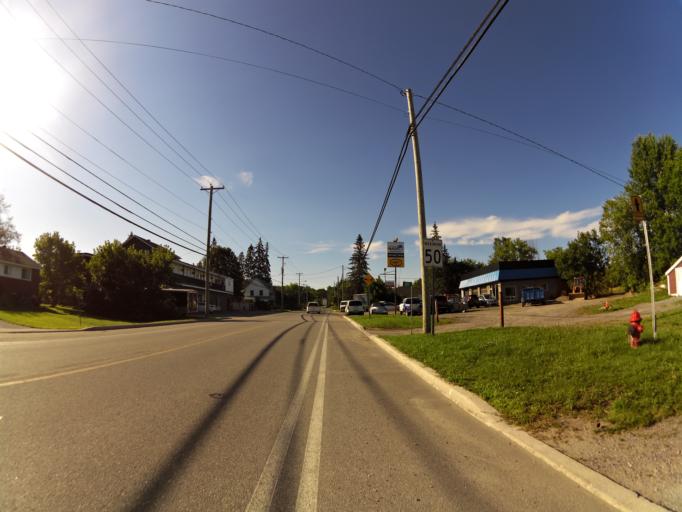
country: CA
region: Quebec
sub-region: Outaouais
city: Gatineau
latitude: 45.5057
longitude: -75.7841
